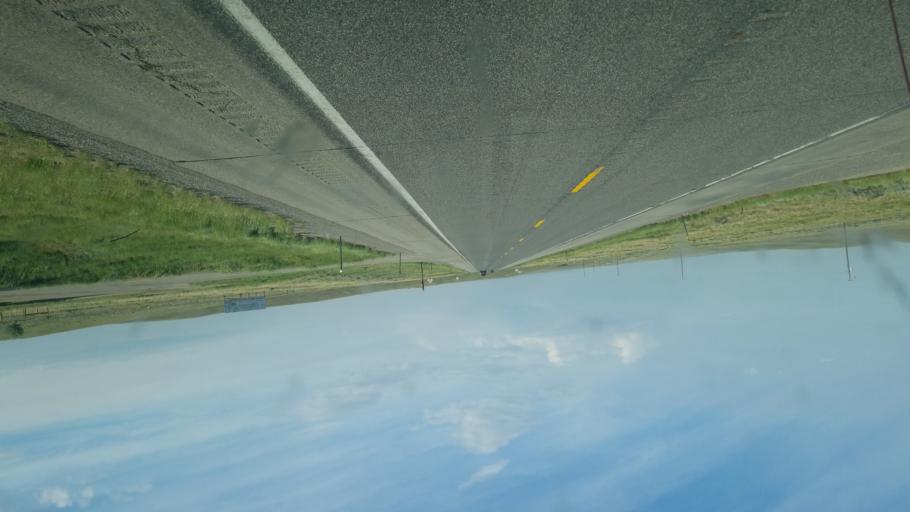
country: US
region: Wyoming
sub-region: Hot Springs County
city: Thermopolis
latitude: 43.1151
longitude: -107.3498
